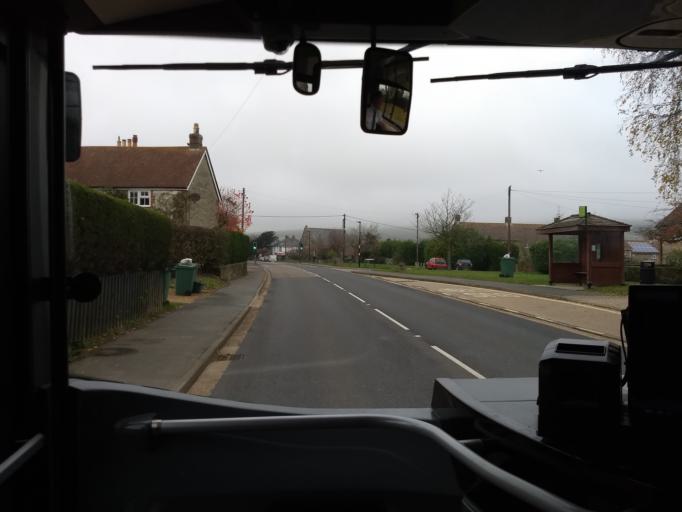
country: GB
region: England
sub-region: Isle of Wight
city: Newchurch
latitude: 50.6700
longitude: -1.2332
